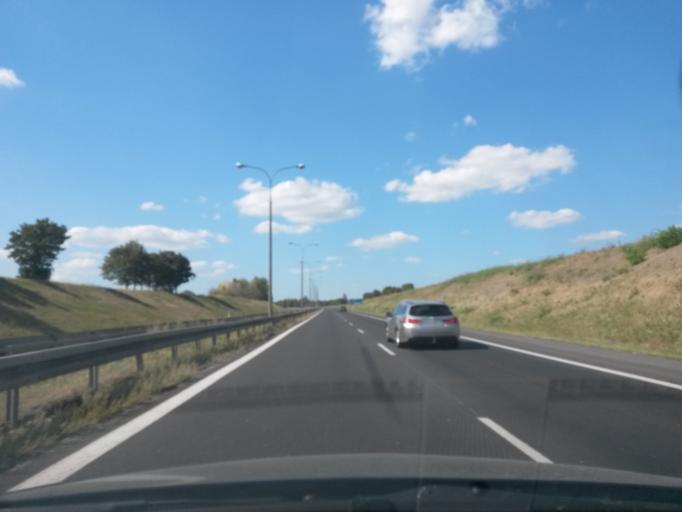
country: PL
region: Masovian Voivodeship
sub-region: Powiat nowodworski
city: Zakroczym
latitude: 52.4349
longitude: 20.6494
